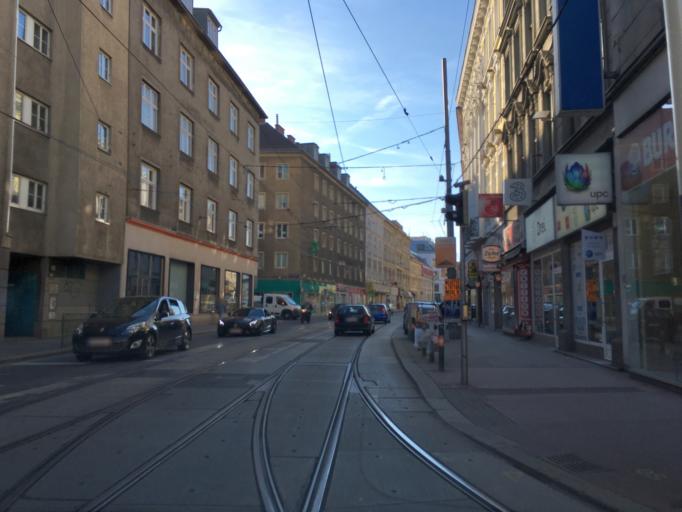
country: AT
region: Vienna
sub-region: Wien Stadt
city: Vienna
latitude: 48.2182
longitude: 16.3309
